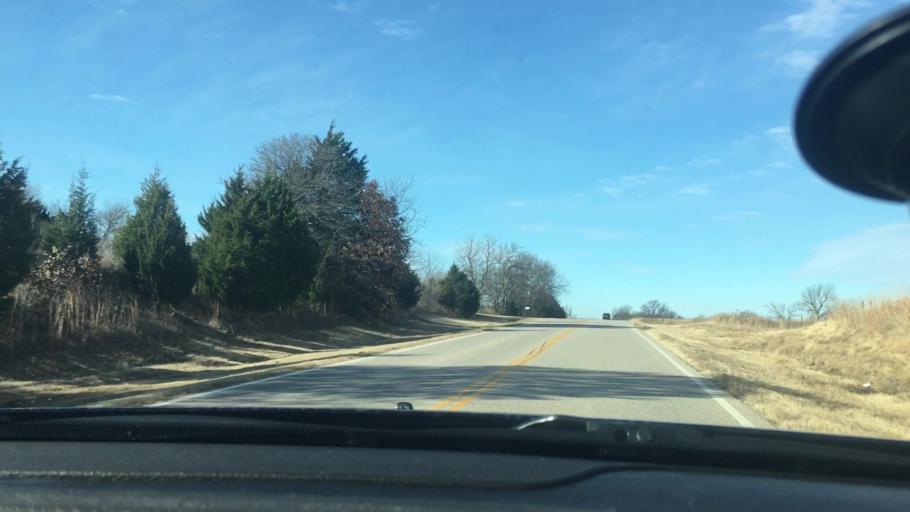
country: US
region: Oklahoma
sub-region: Garvin County
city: Stratford
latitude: 34.9860
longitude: -96.9891
